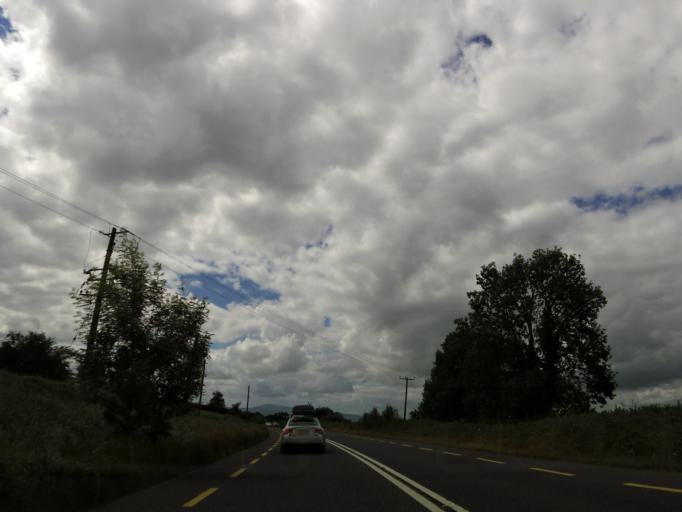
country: IE
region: Munster
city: Nenagh Bridge
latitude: 52.9207
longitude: -8.1736
